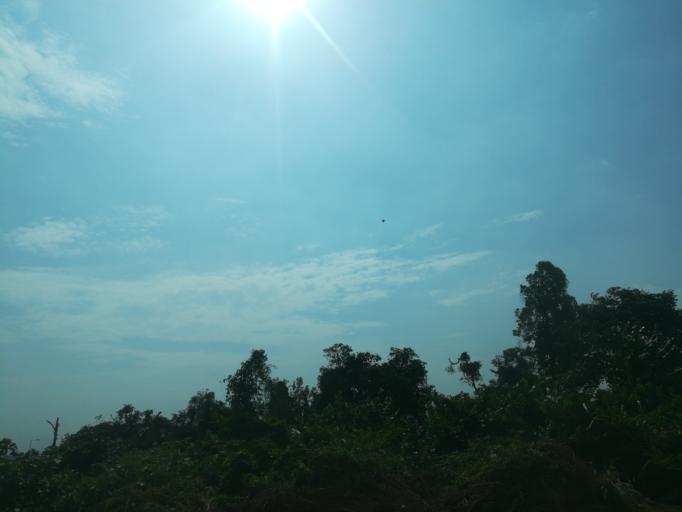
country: NG
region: Lagos
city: Ikorodu
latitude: 6.6380
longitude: 3.6700
